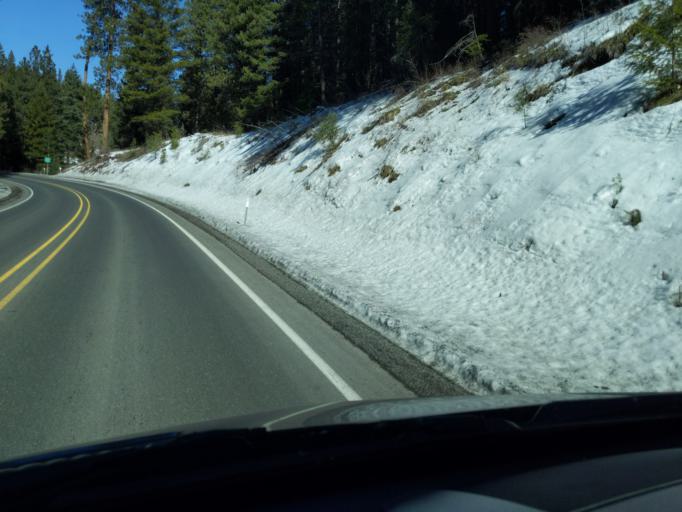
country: US
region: Oregon
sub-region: Grant County
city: John Day
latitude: 44.8881
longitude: -119.0115
